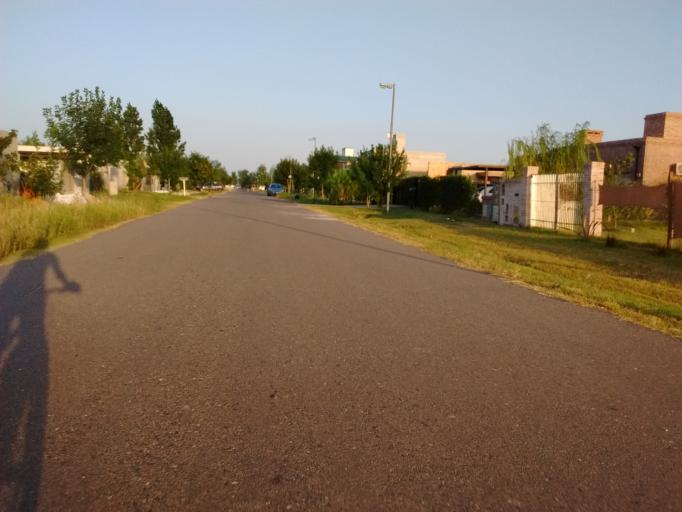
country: AR
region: Santa Fe
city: Funes
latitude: -32.9158
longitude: -60.7760
